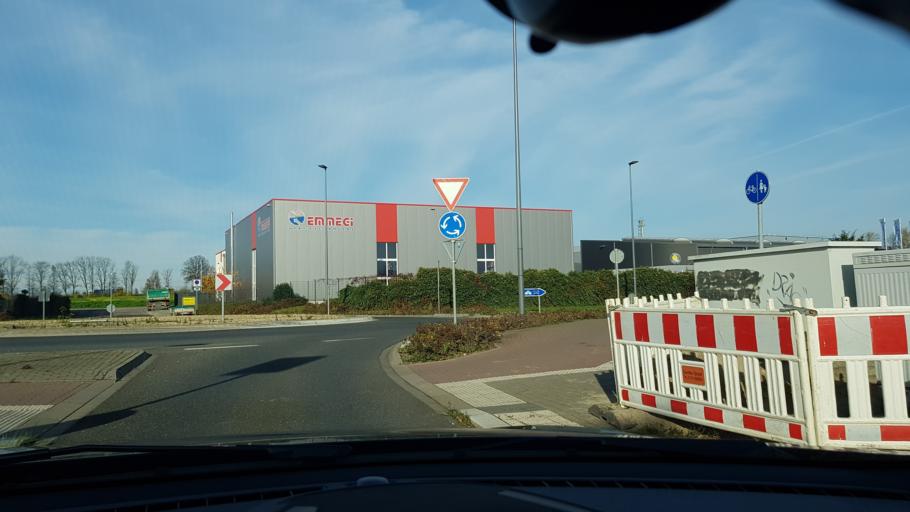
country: DE
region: North Rhine-Westphalia
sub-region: Regierungsbezirk Dusseldorf
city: Neubrueck
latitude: 51.1304
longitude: 6.6125
